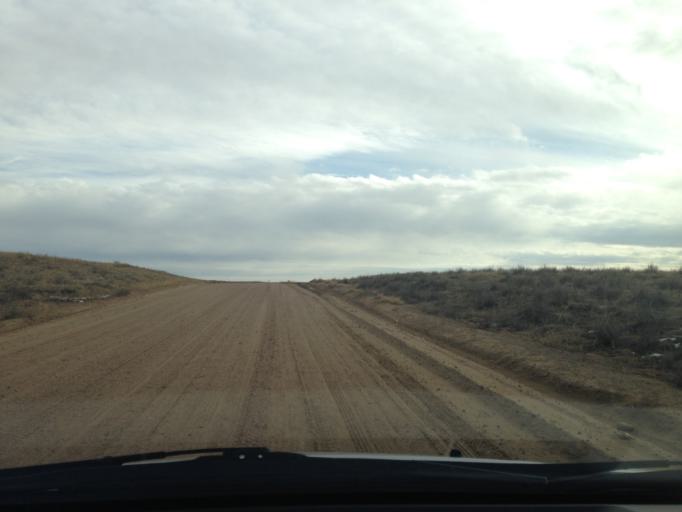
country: US
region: Colorado
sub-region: Weld County
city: Keenesburg
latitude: 40.2506
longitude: -104.2068
